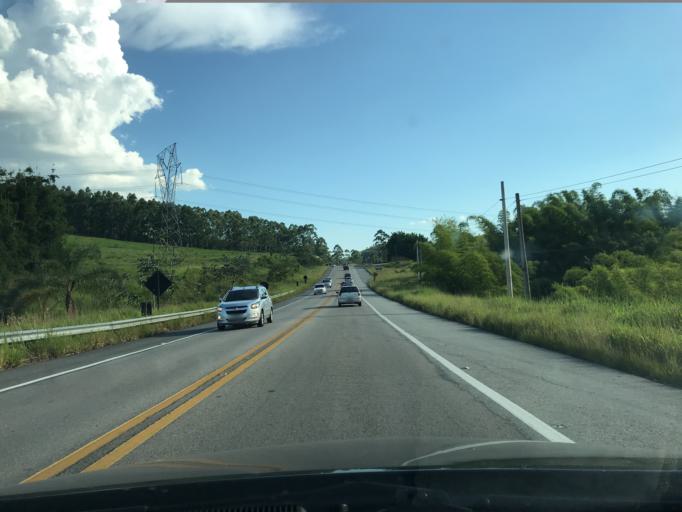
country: BR
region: Sao Paulo
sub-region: Tremembe
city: Tremembe
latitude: -22.8985
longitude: -45.5878
